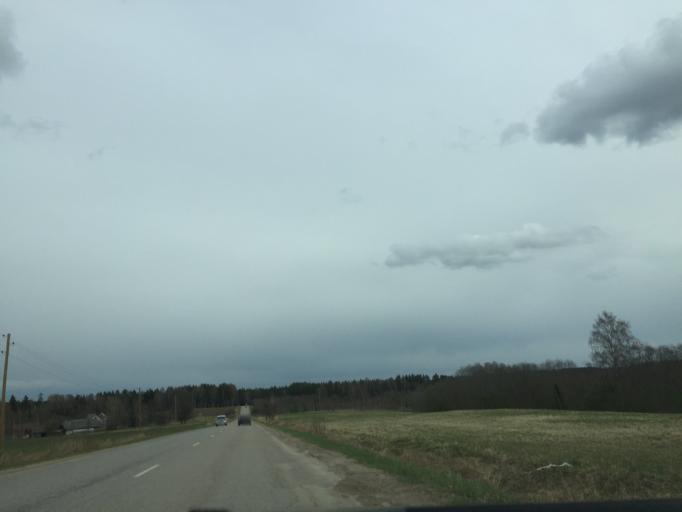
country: LV
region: Priekuli
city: Priekuli
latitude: 57.3217
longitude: 25.3758
